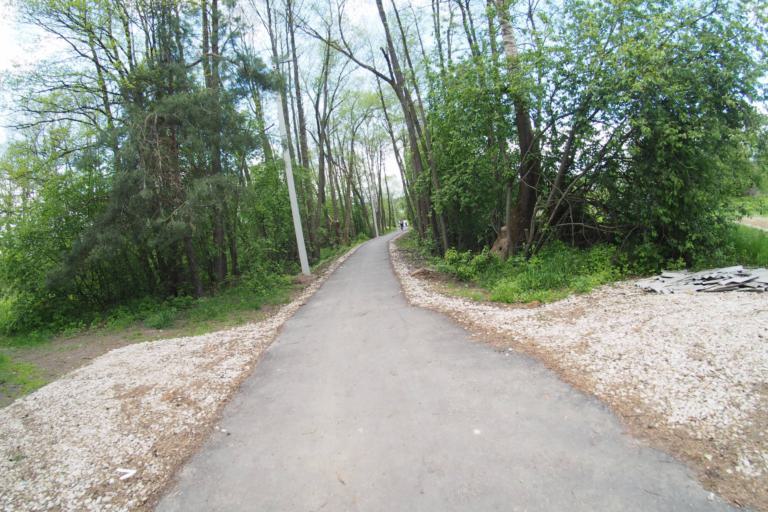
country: RU
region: Moskovskaya
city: Rechitsy
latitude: 55.5400
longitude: 38.4337
